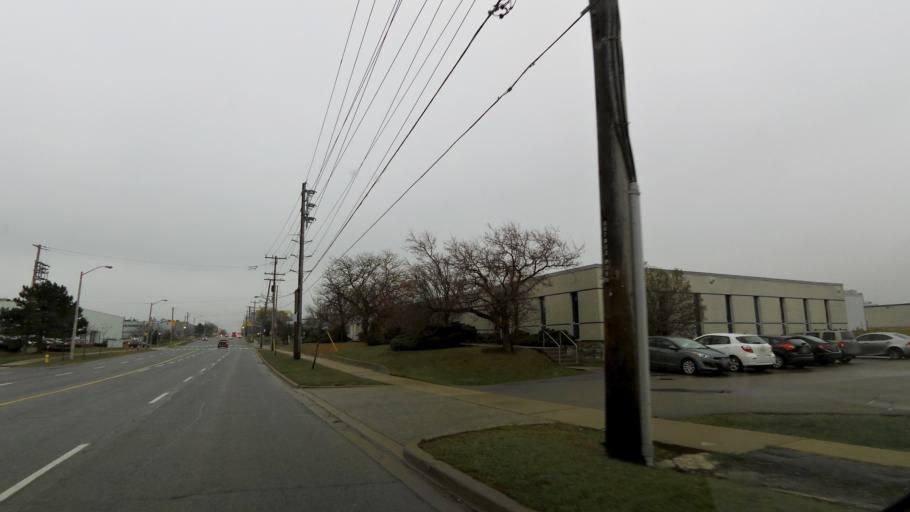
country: CA
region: Ontario
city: Etobicoke
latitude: 43.6947
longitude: -79.5992
